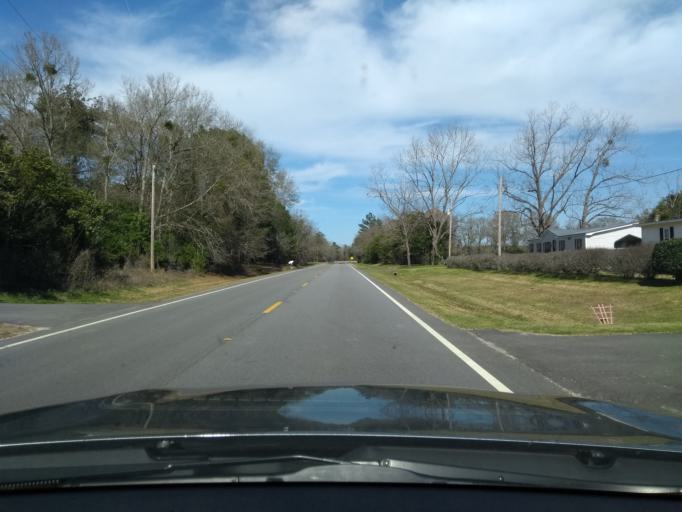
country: US
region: Georgia
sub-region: Bulloch County
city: Brooklet
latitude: 32.4757
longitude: -81.6040
